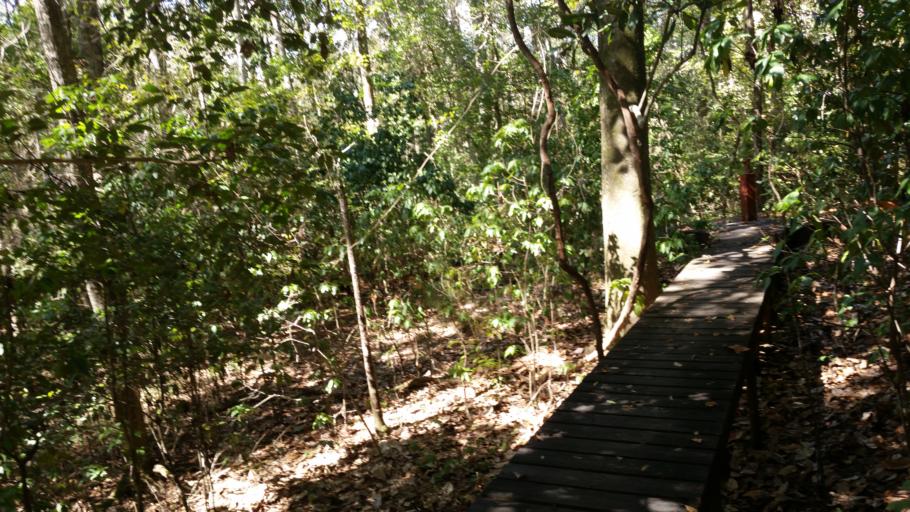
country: US
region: Alabama
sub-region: Baldwin County
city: Spanish Fort
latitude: 30.7374
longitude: -87.9247
